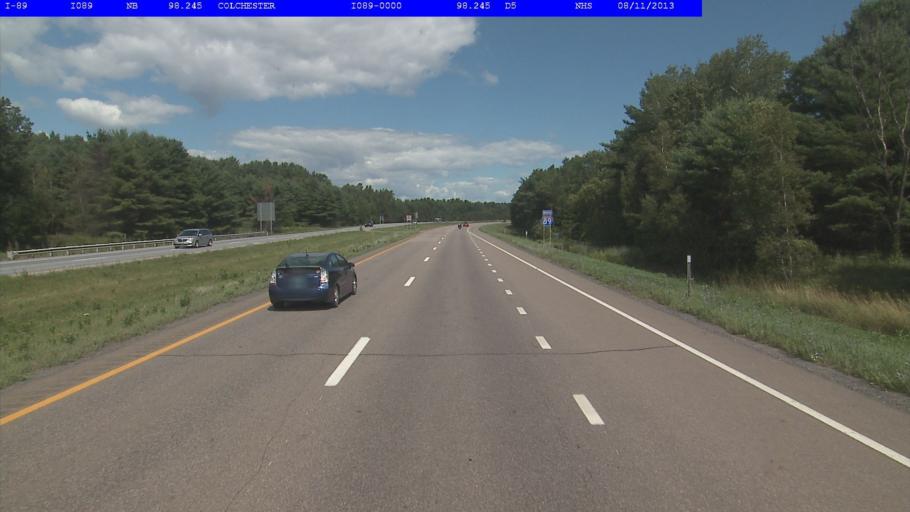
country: US
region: Vermont
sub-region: Chittenden County
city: Colchester
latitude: 44.5949
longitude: -73.1715
